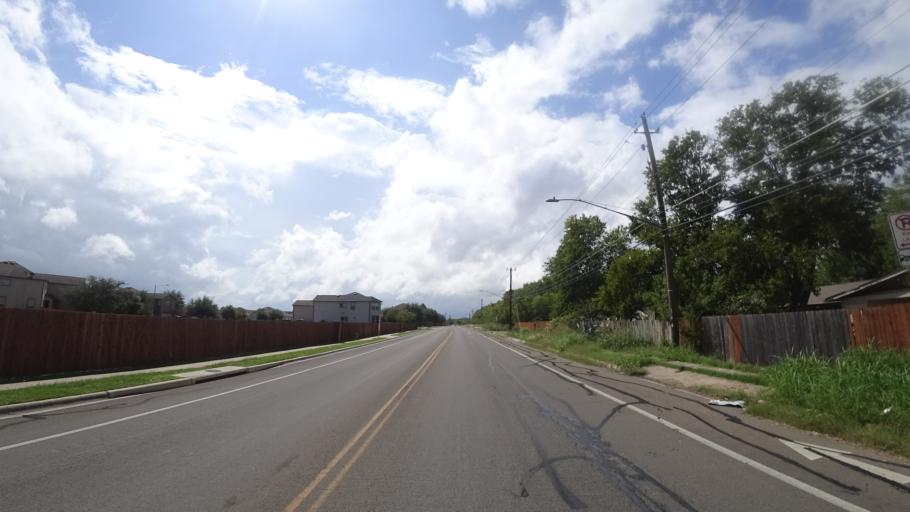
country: US
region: Texas
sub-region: Travis County
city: Onion Creek
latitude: 30.1614
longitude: -97.7441
